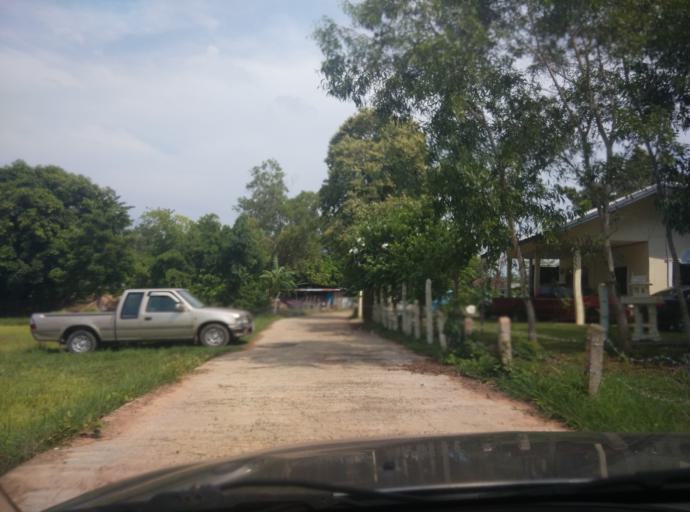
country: TH
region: Sisaket
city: Huai Thap Than
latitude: 15.0505
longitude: 104.0852
